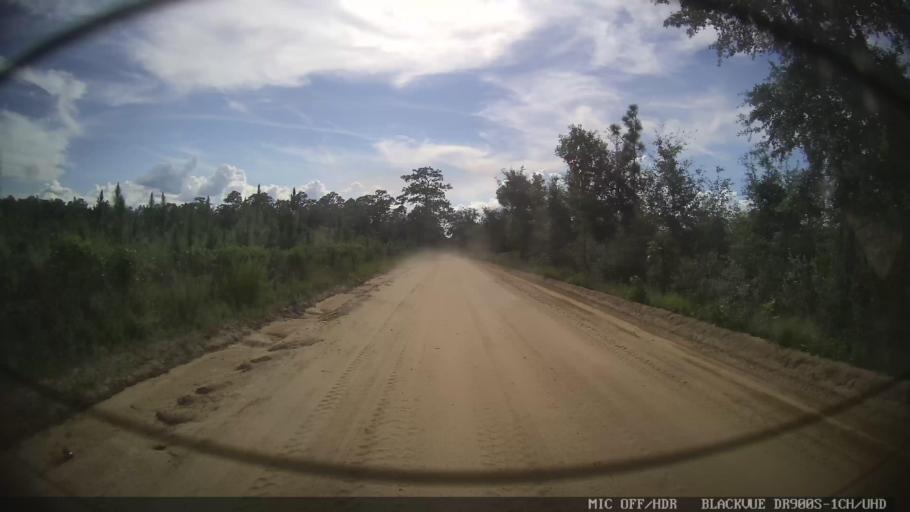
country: US
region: Georgia
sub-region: Echols County
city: Statenville
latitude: 30.6245
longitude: -83.1938
